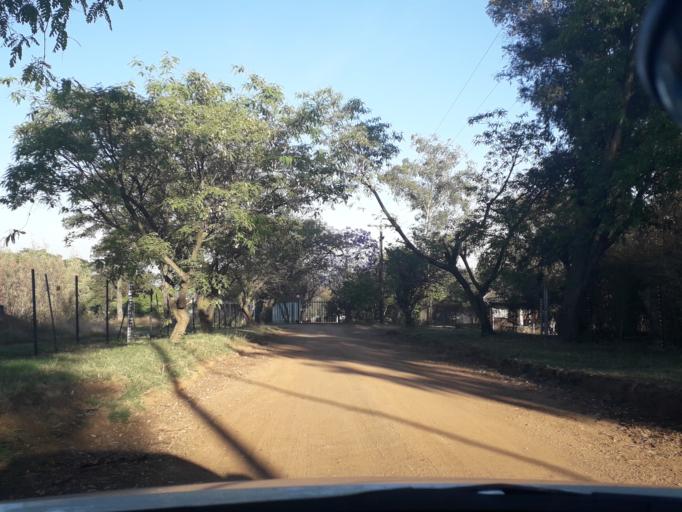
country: ZA
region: Gauteng
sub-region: West Rand District Municipality
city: Muldersdriseloop
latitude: -26.0532
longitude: 27.8830
